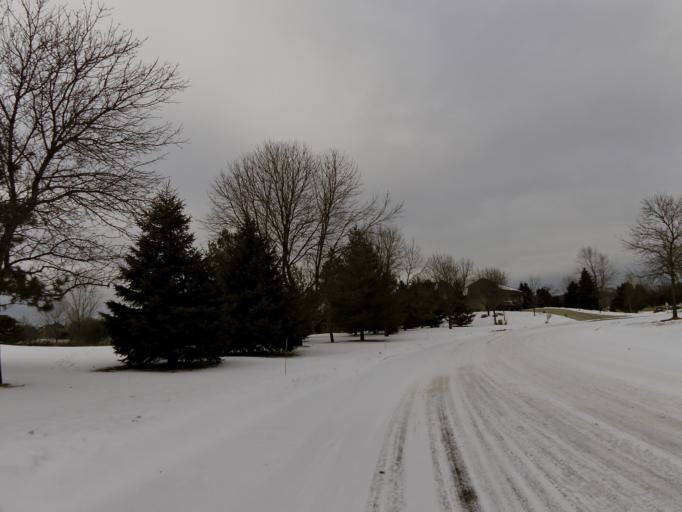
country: US
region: Minnesota
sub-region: Washington County
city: Lake Elmo
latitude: 44.9620
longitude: -92.8563
